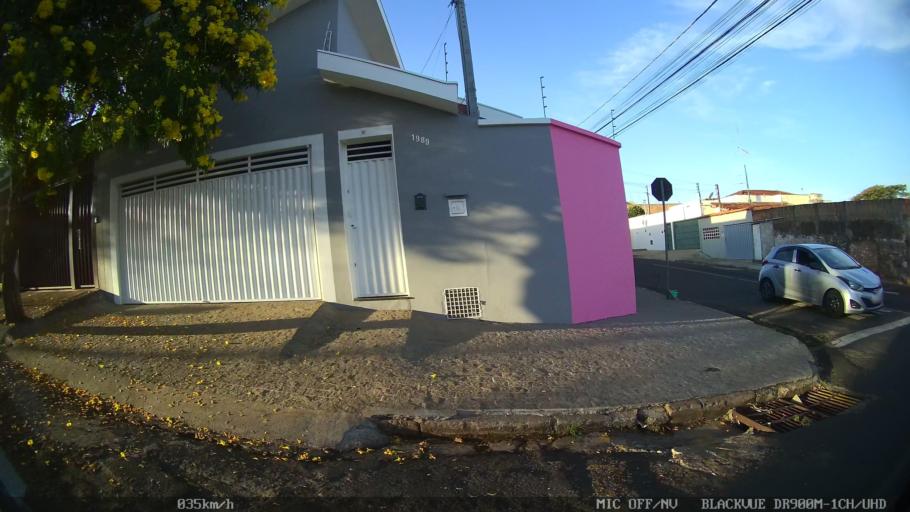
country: BR
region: Sao Paulo
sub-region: Franca
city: Franca
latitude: -20.5300
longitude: -47.3887
